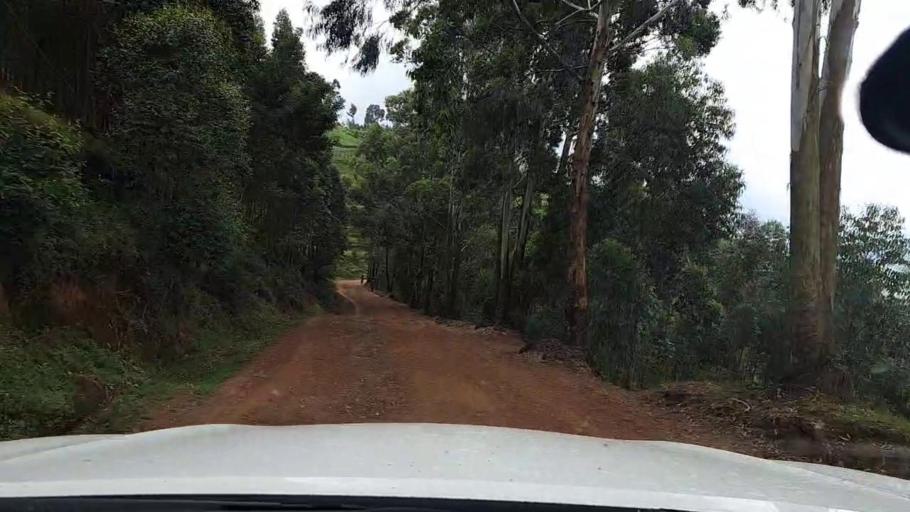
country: RW
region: Western Province
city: Kibuye
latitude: -2.1699
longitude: 29.4250
